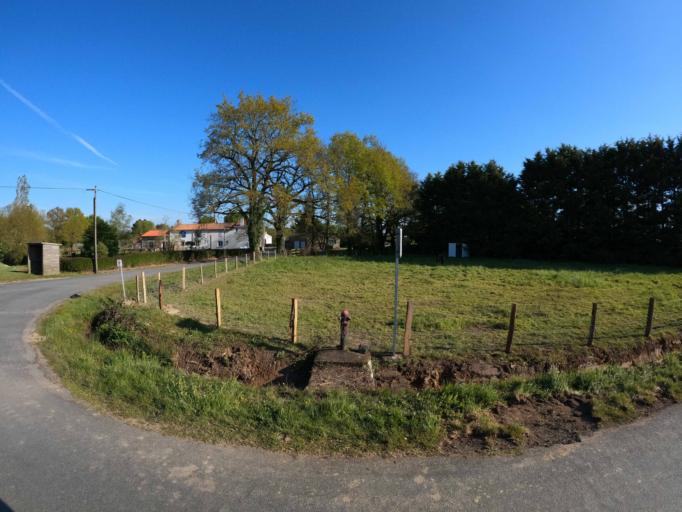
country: FR
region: Pays de la Loire
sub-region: Departement de la Vendee
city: Les Brouzils
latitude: 46.8910
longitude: -1.3508
